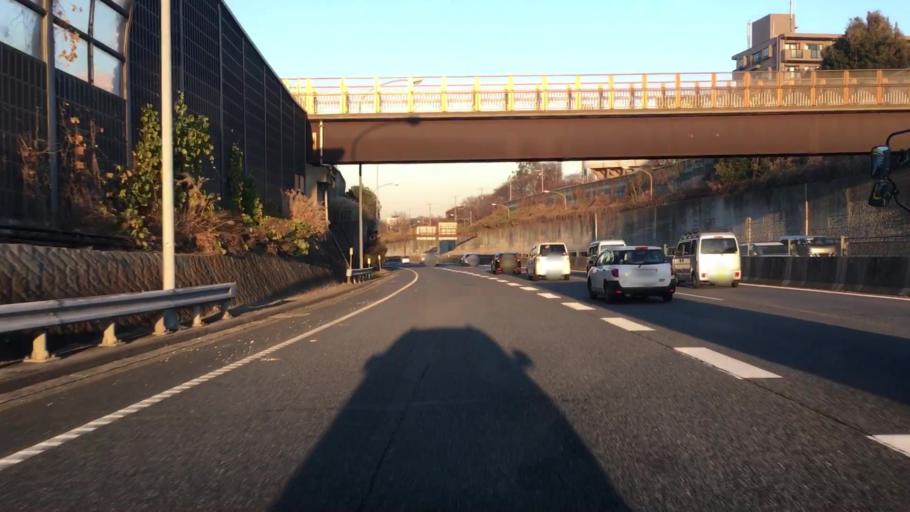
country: JP
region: Kanagawa
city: Yokohama
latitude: 35.4539
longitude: 139.5787
